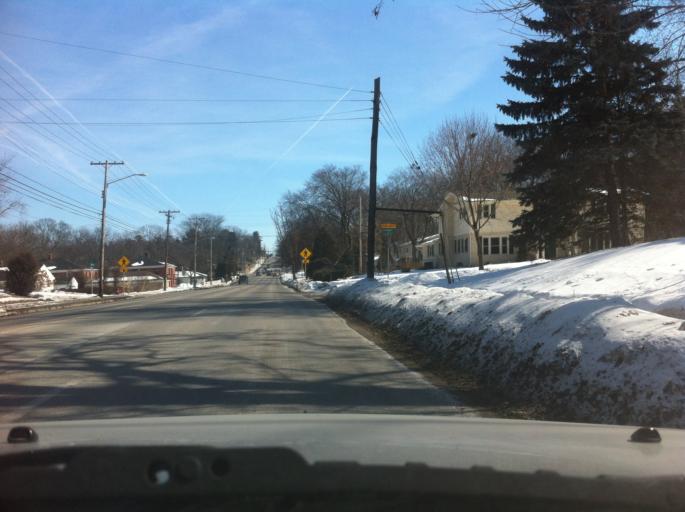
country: US
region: Wisconsin
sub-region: Dane County
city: Shorewood Hills
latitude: 43.0609
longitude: -89.4589
